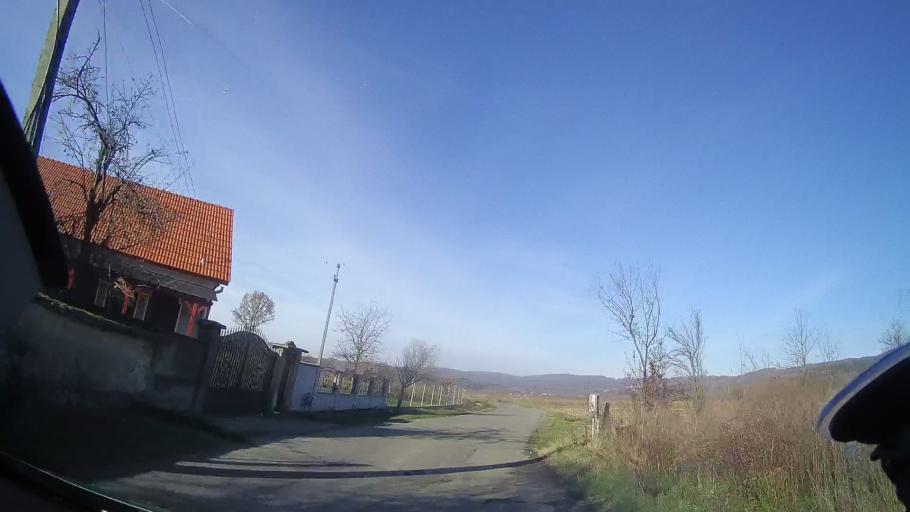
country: RO
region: Bihor
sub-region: Comuna Auseu
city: Auseu
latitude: 47.0252
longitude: 22.4866
